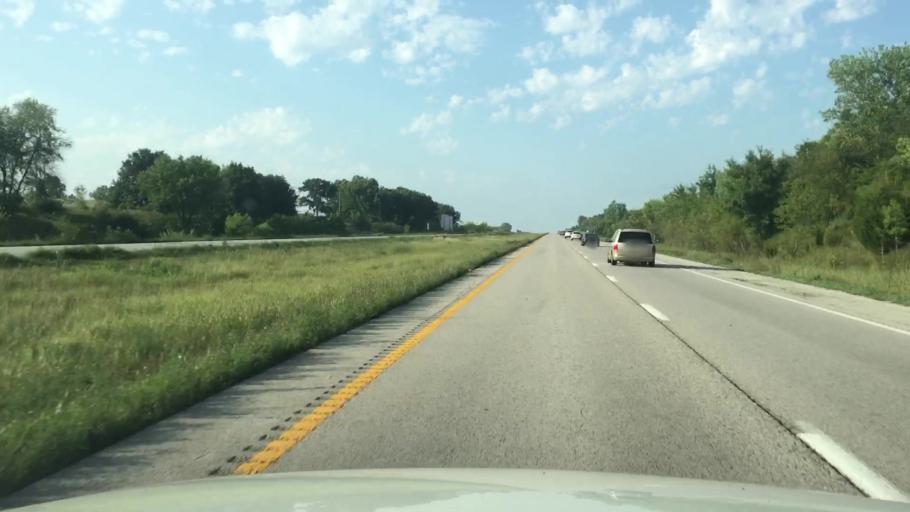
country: US
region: Missouri
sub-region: Clinton County
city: Cameron
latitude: 39.6855
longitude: -94.2311
